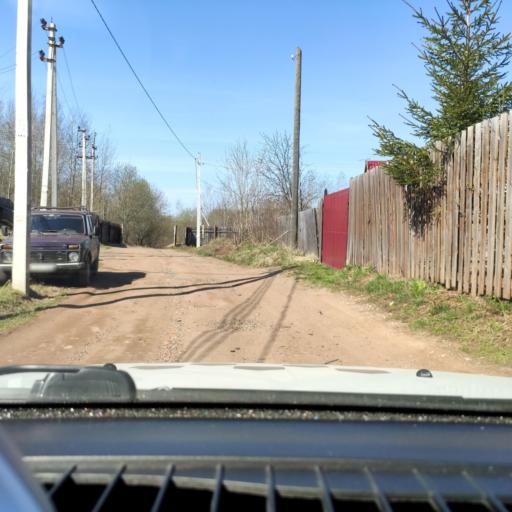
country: RU
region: Perm
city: Perm
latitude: 58.0687
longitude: 56.3750
